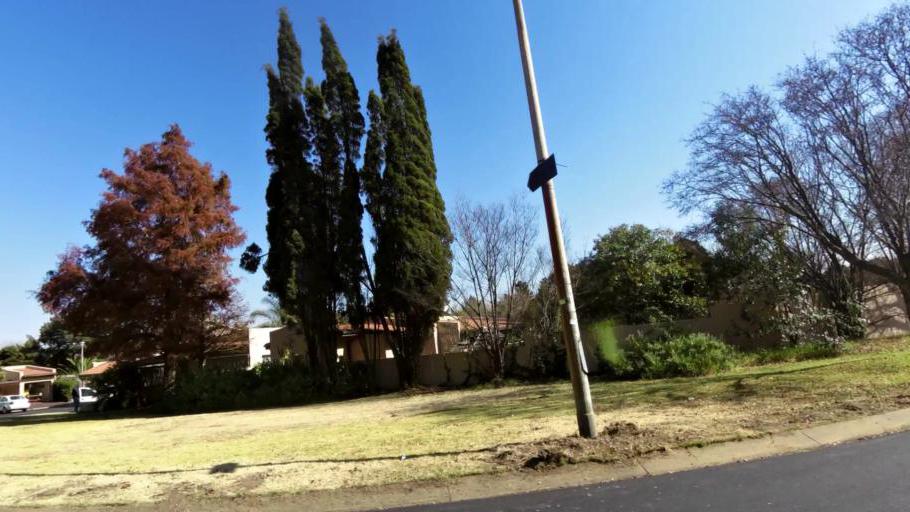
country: ZA
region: Gauteng
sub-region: City of Johannesburg Metropolitan Municipality
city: Johannesburg
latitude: -26.2475
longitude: 27.9924
